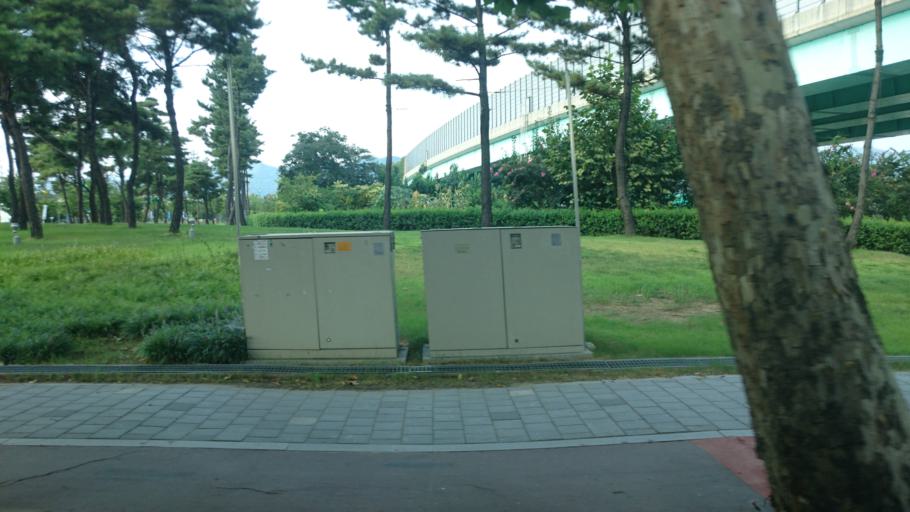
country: KR
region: Gyeongsangbuk-do
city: Gyeongsan-si
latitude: 35.8753
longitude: 128.6849
